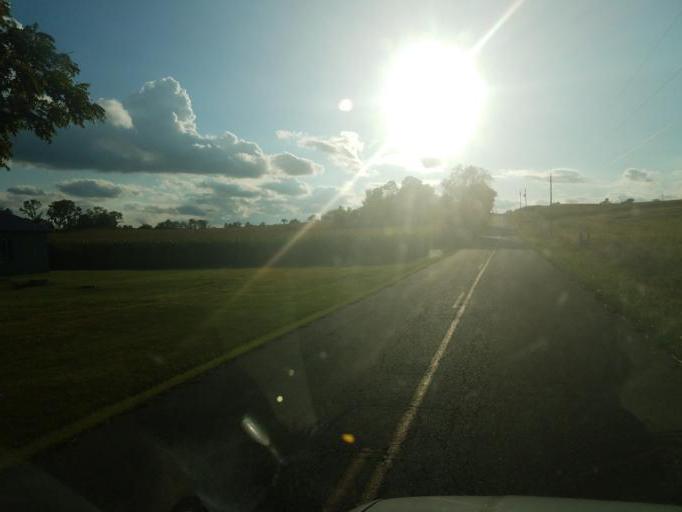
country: US
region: Ohio
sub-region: Knox County
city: Fredericktown
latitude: 40.4241
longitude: -82.5960
